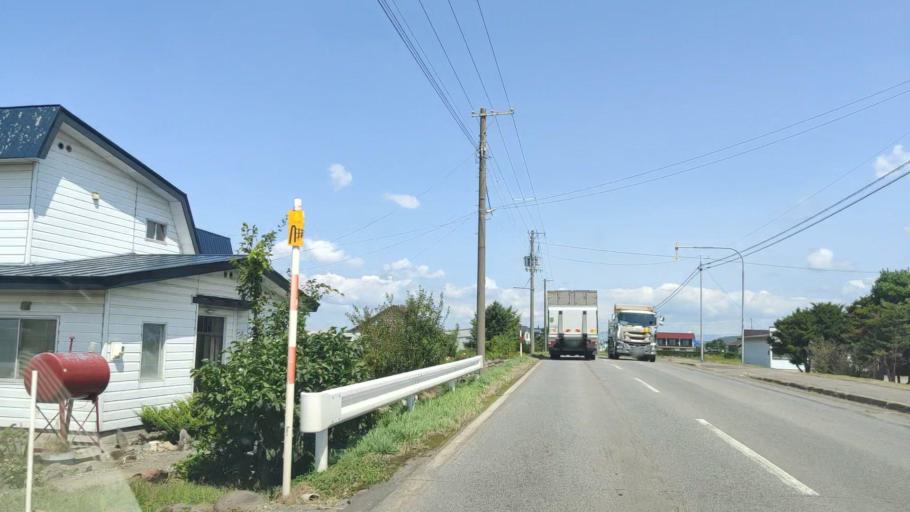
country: JP
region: Hokkaido
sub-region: Asahikawa-shi
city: Asahikawa
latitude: 43.7213
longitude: 142.4579
